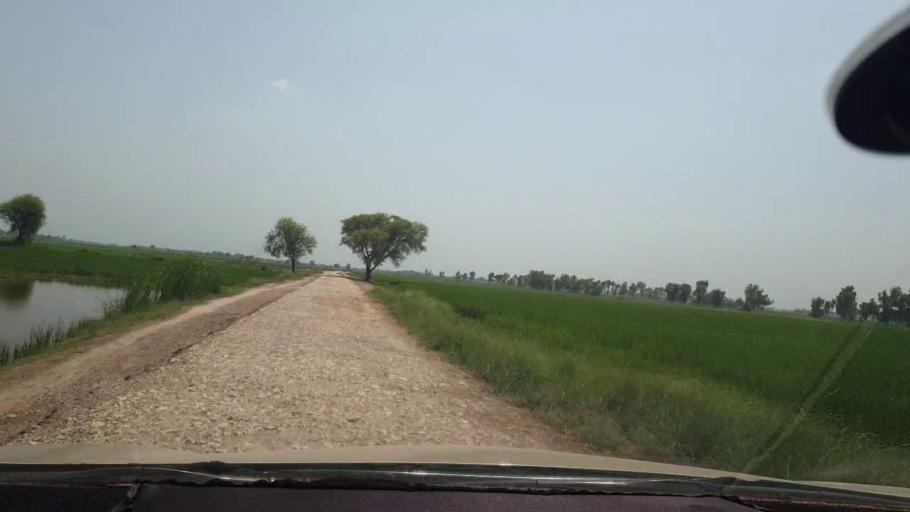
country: PK
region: Sindh
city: Kambar
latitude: 27.6542
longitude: 67.9310
